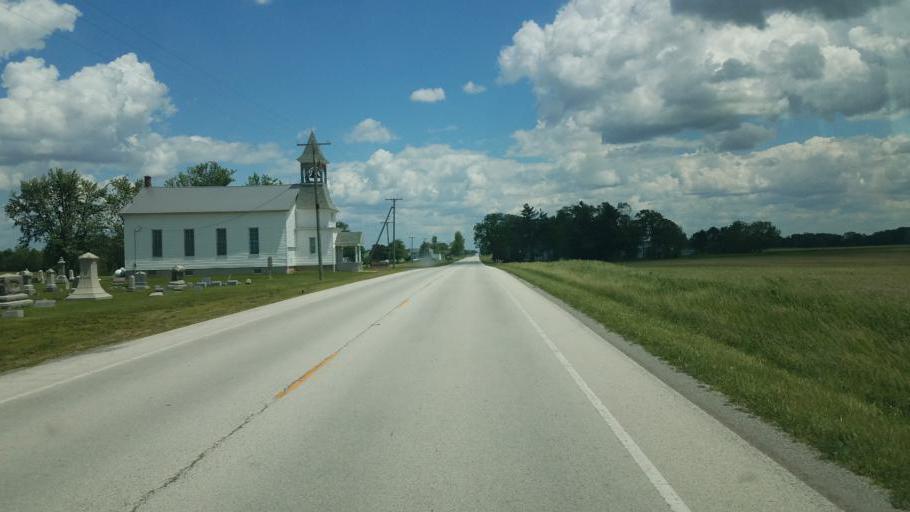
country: US
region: Ohio
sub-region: Wyandot County
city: Upper Sandusky
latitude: 40.8405
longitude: -83.1933
